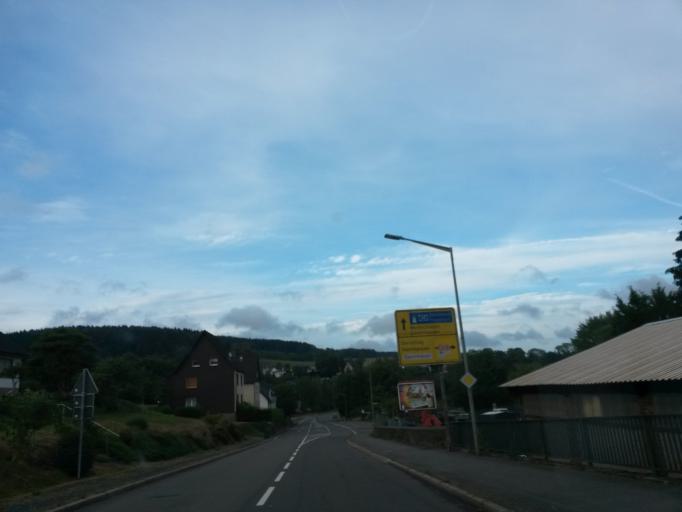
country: DE
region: North Rhine-Westphalia
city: Bergneustadt
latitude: 51.0534
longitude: 7.6268
